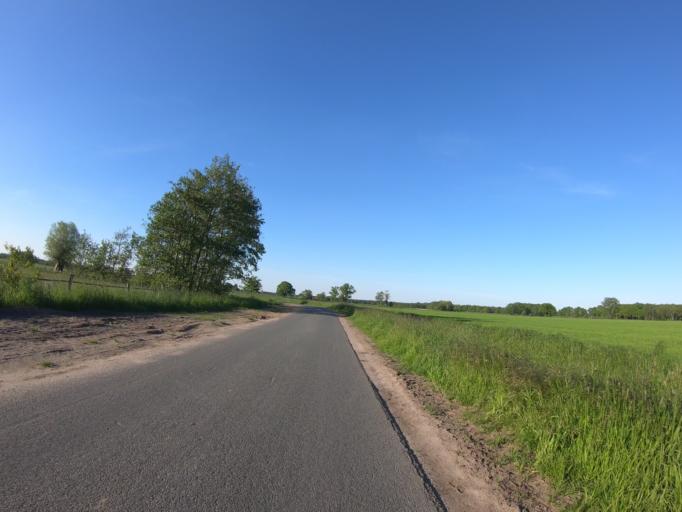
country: DE
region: Lower Saxony
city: Wagenhoff
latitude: 52.5263
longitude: 10.5589
